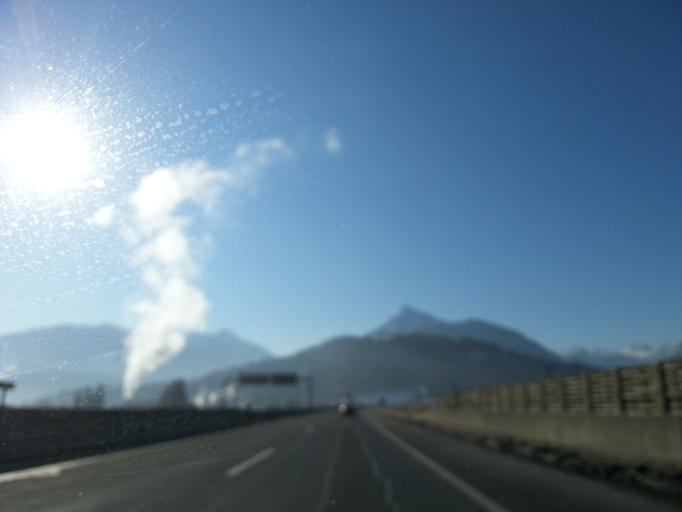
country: AT
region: Salzburg
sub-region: Politischer Bezirk Sankt Johann im Pongau
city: Eben im Pongau
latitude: 47.3896
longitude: 13.3996
